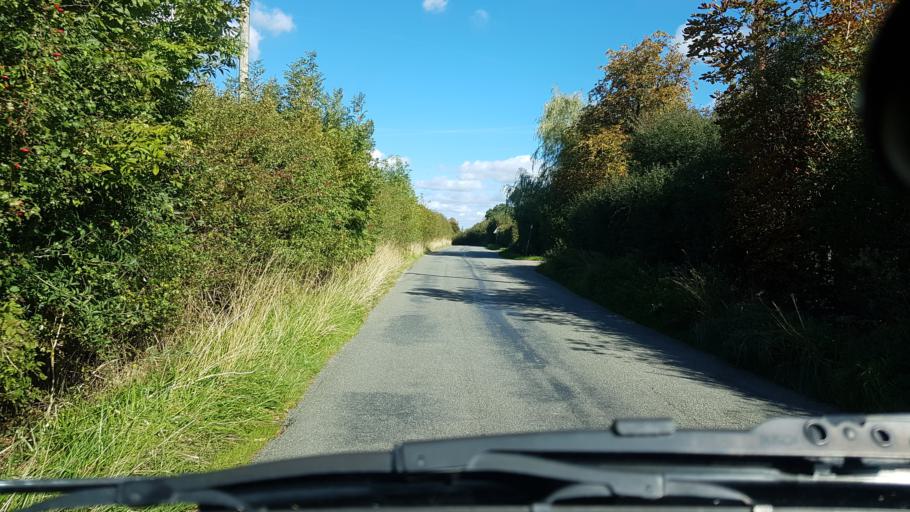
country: GB
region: England
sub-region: West Sussex
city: Billingshurst
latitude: 51.0005
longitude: -0.4313
